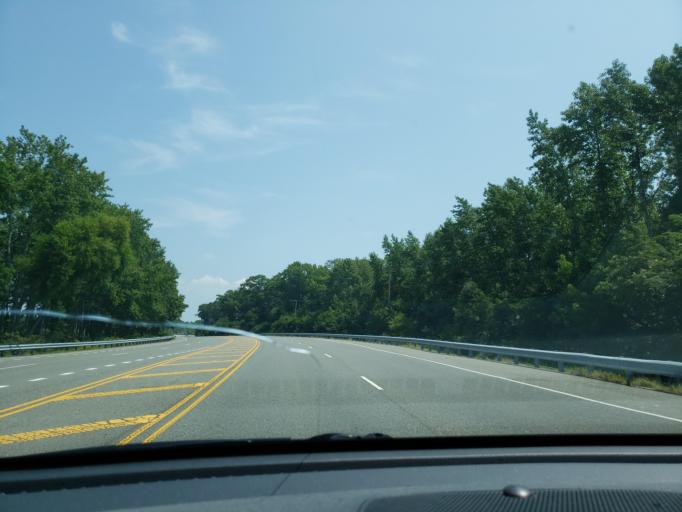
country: US
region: New Jersey
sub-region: Cape May County
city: North Cape May
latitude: 38.9731
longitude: -74.9411
